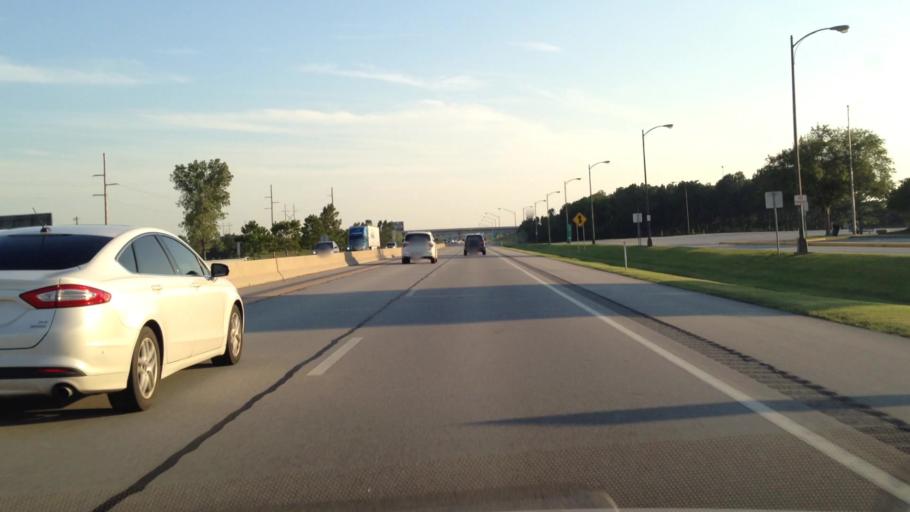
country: US
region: Oklahoma
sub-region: Ottawa County
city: Miami
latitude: 36.8759
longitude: -94.8452
